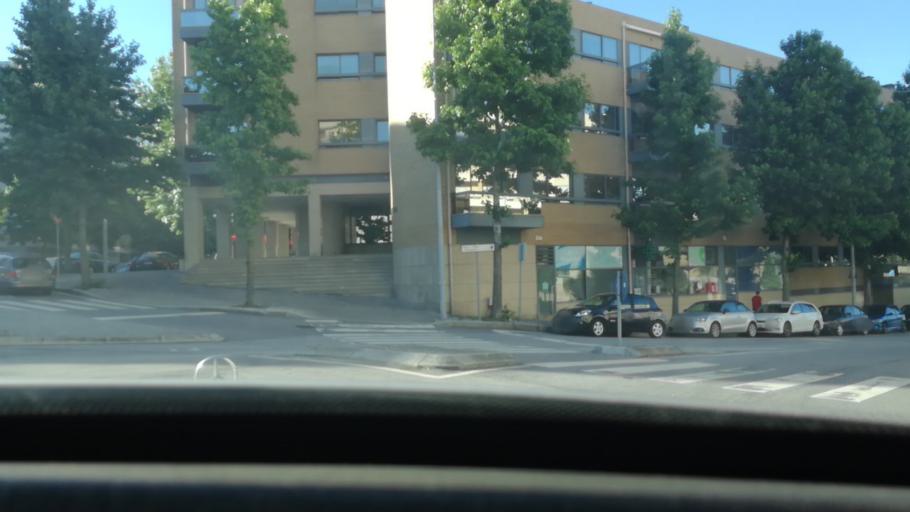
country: PT
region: Porto
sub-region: Maia
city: Maia
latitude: 41.2307
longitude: -8.6132
